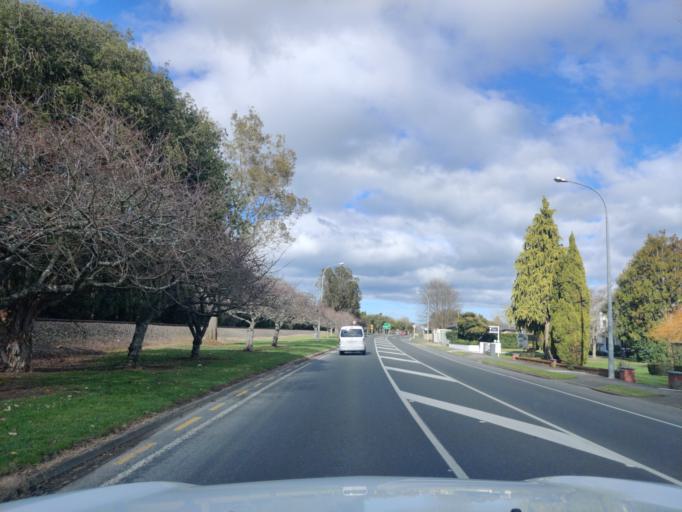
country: NZ
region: Waikato
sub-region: Matamata-Piako District
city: Matamata
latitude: -37.8219
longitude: 175.7711
